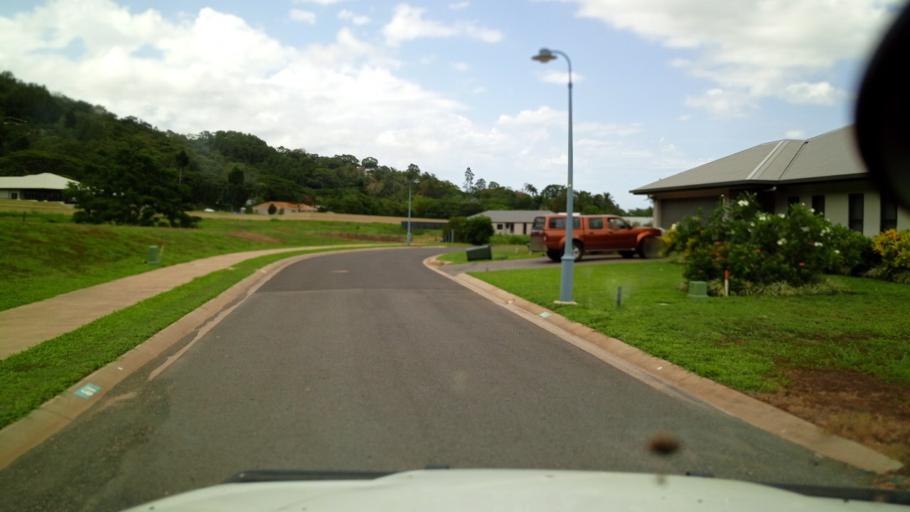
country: AU
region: Queensland
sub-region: Cairns
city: Redlynch
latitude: -16.8998
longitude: 145.6923
